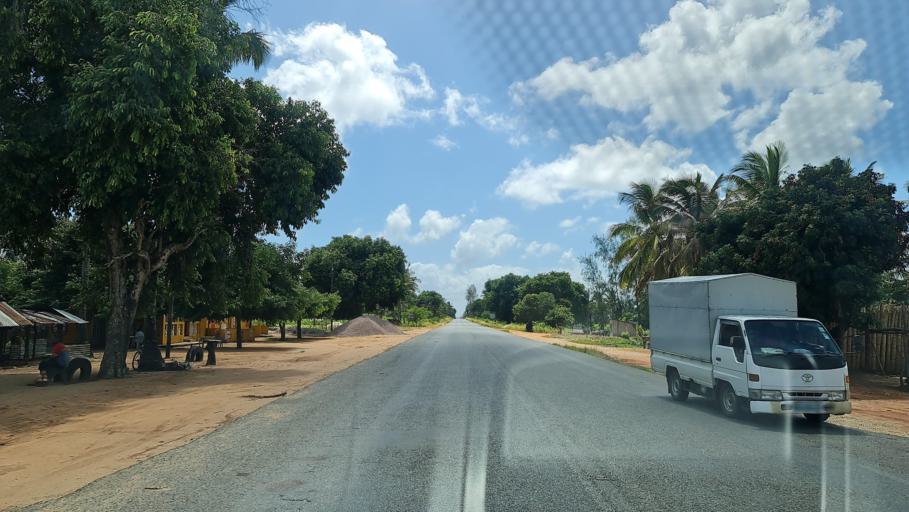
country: MZ
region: Inhambane
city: Maxixe
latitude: -24.5288
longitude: 34.9527
